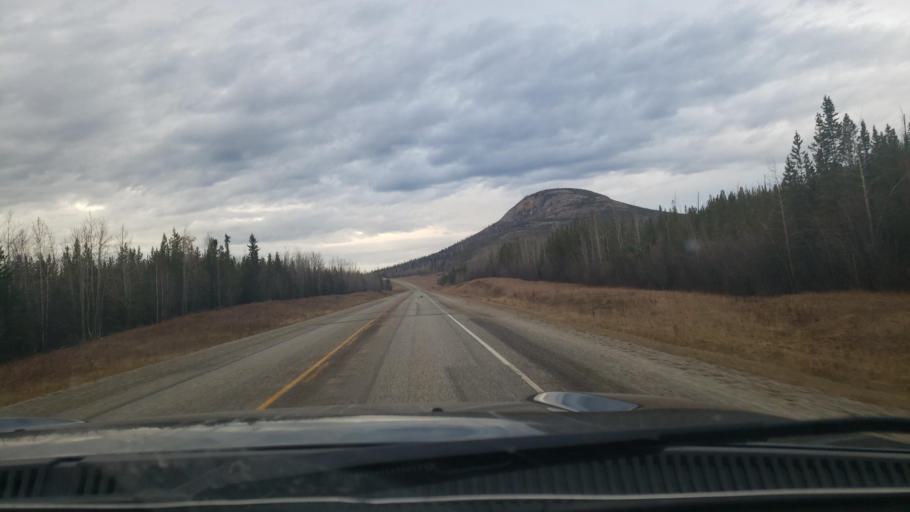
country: CA
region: Yukon
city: Watson Lake
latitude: 59.9146
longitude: -127.4392
